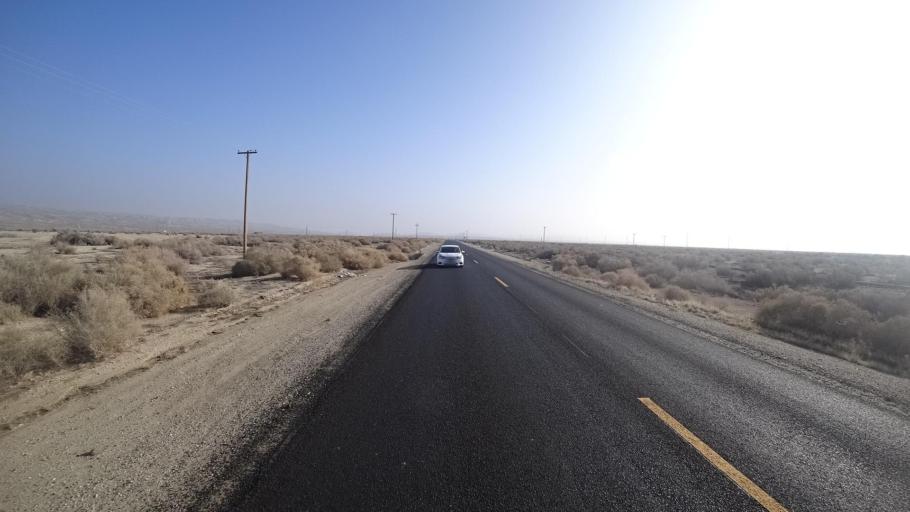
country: US
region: California
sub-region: Kern County
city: Ford City
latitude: 35.1805
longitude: -119.4941
